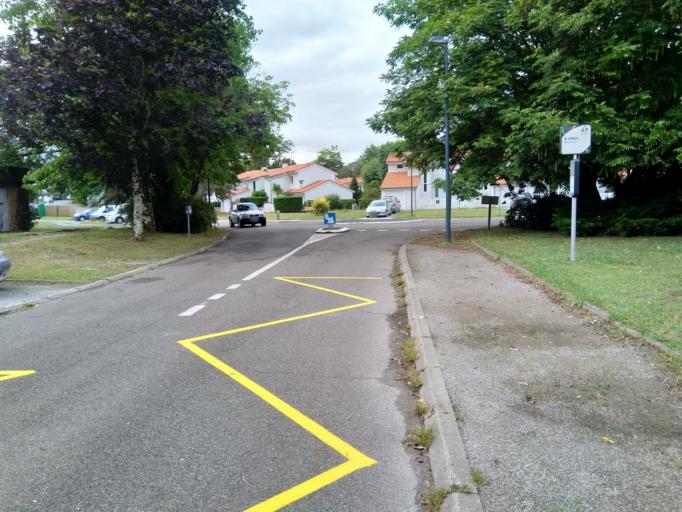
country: FR
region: Aquitaine
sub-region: Departement des Landes
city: Dax
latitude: 43.7128
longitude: -1.0417
